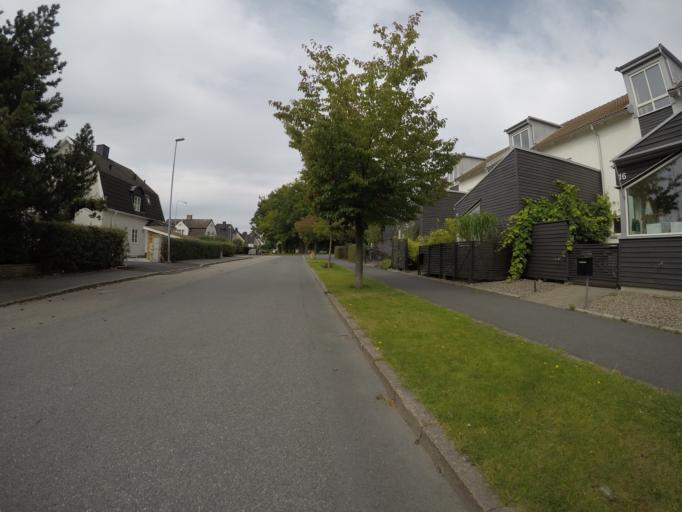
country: SE
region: Joenkoeping
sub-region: Jonkopings Kommun
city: Jonkoping
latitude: 57.7846
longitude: 14.2196
